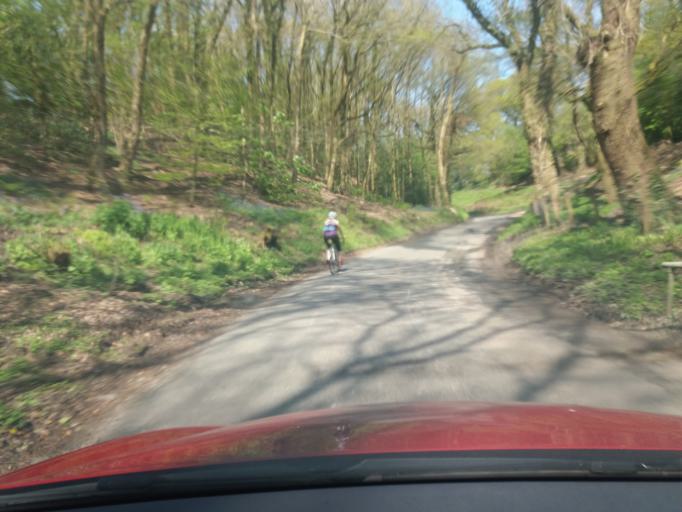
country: GB
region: England
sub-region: Lancashire
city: Chorley
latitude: 53.6896
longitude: -2.6191
